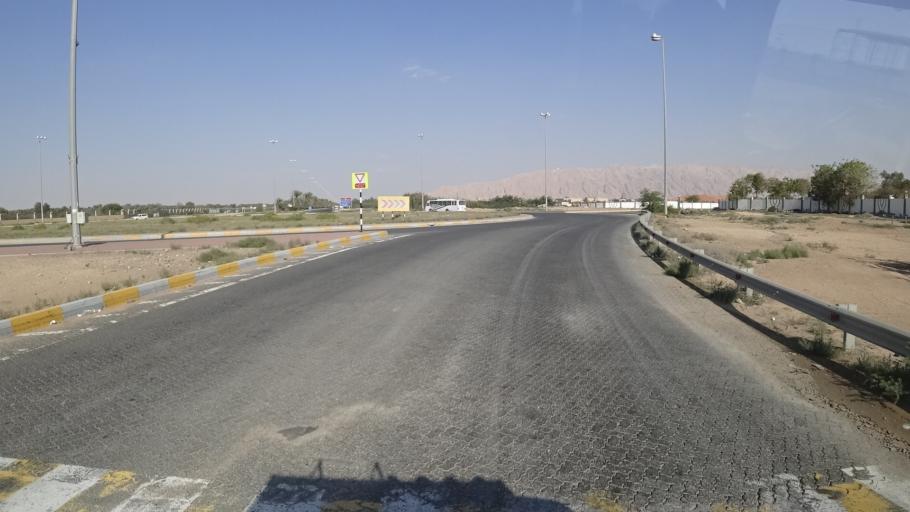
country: AE
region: Abu Dhabi
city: Al Ain
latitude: 24.0791
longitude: 55.6635
